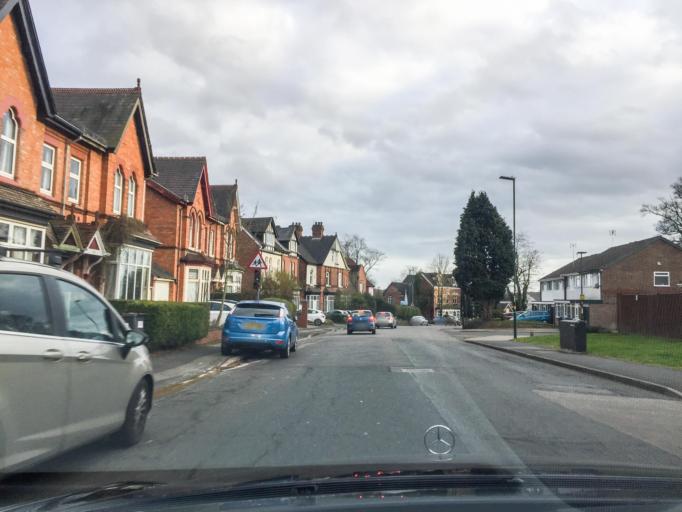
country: GB
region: England
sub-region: City and Borough of Birmingham
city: Bartley Green
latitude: 52.4120
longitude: -1.9608
